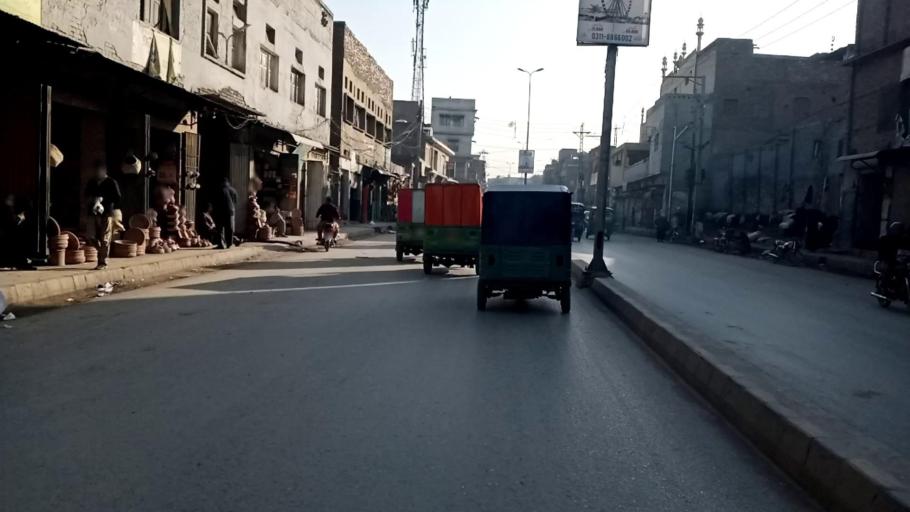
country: PK
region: Khyber Pakhtunkhwa
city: Peshawar
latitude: 34.0071
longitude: 71.5847
